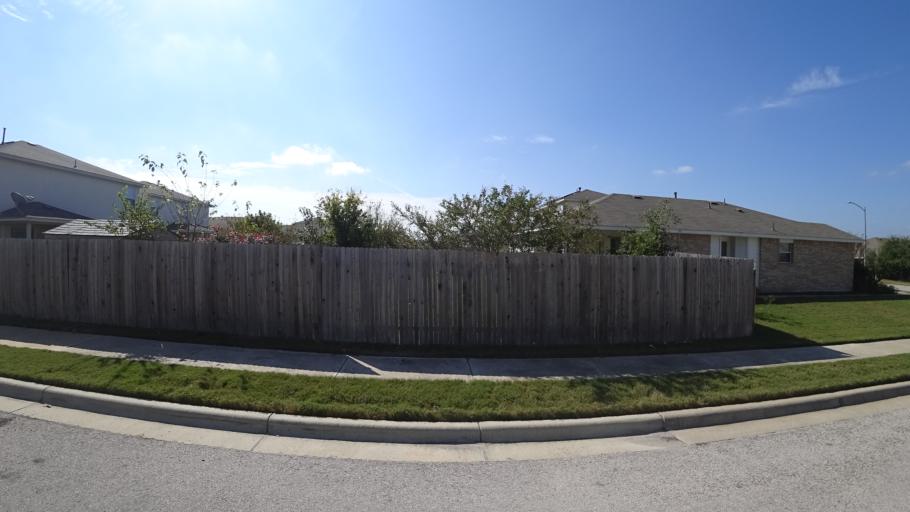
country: US
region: Texas
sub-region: Travis County
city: Pflugerville
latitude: 30.4230
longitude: -97.6337
